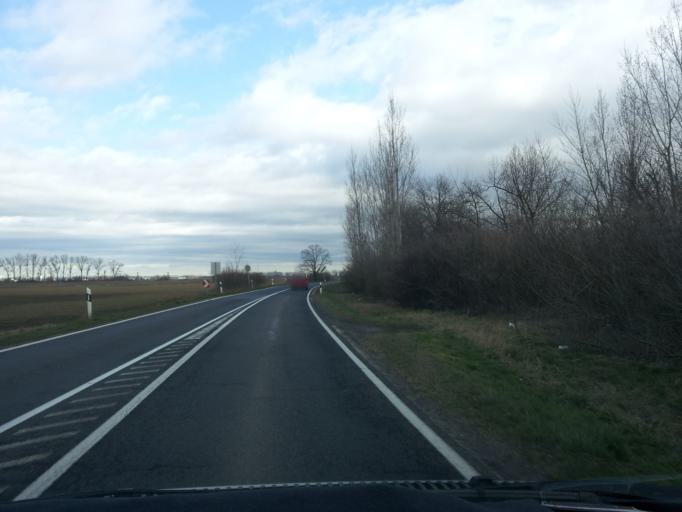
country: HU
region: Vas
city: Gencsapati
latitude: 47.2724
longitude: 16.6077
